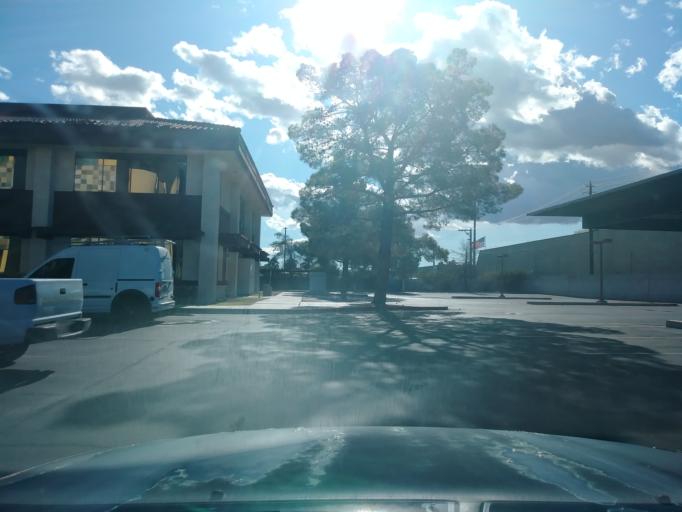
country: US
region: Nevada
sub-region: Clark County
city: Spring Valley
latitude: 36.1459
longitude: -115.2240
